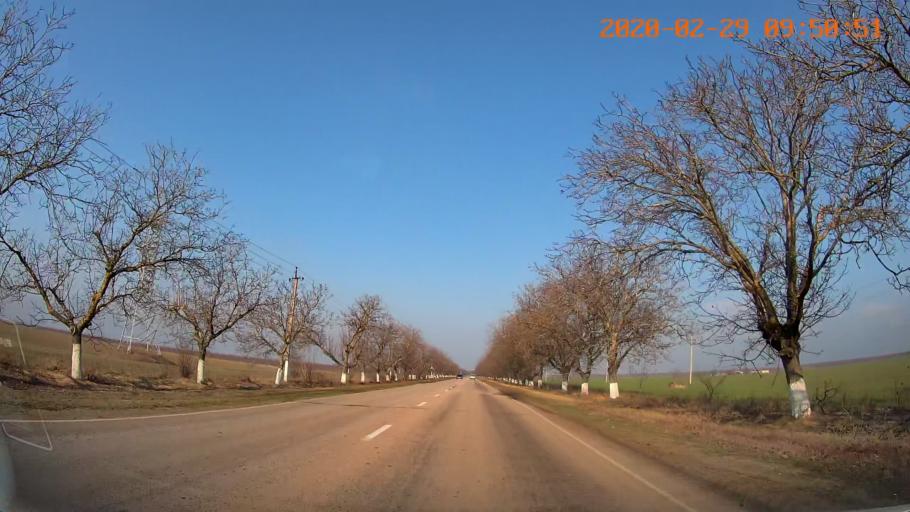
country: MD
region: Telenesti
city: Slobozia
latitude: 46.7039
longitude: 29.7487
